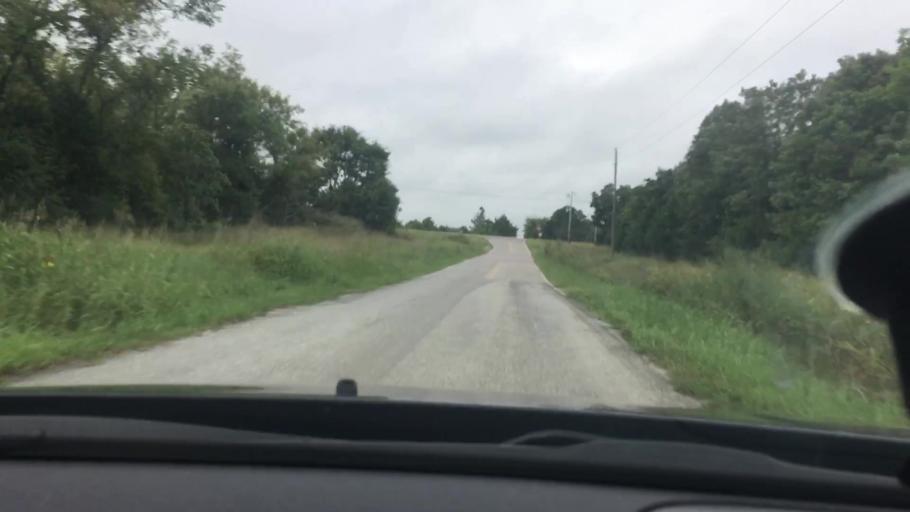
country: US
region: Oklahoma
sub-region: Pontotoc County
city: Byng
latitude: 34.8000
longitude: -96.5475
